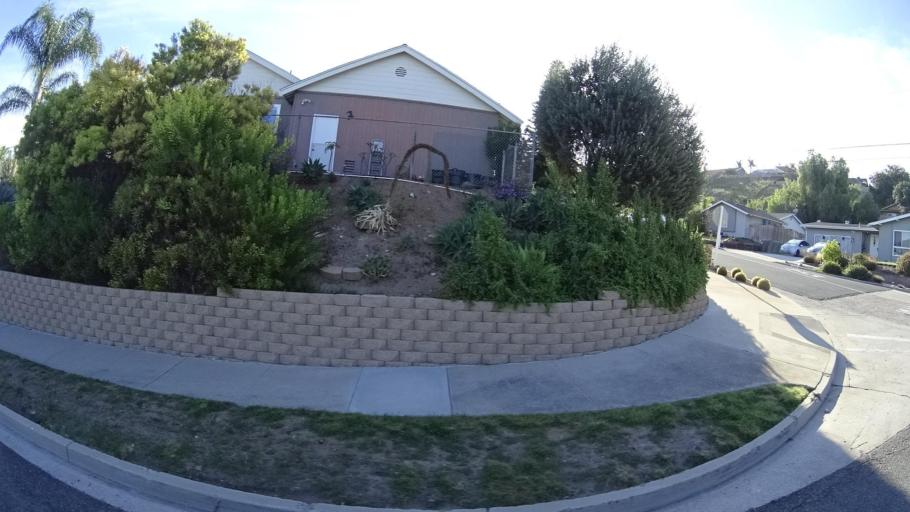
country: US
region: California
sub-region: San Diego County
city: Spring Valley
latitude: 32.7422
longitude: -116.9790
